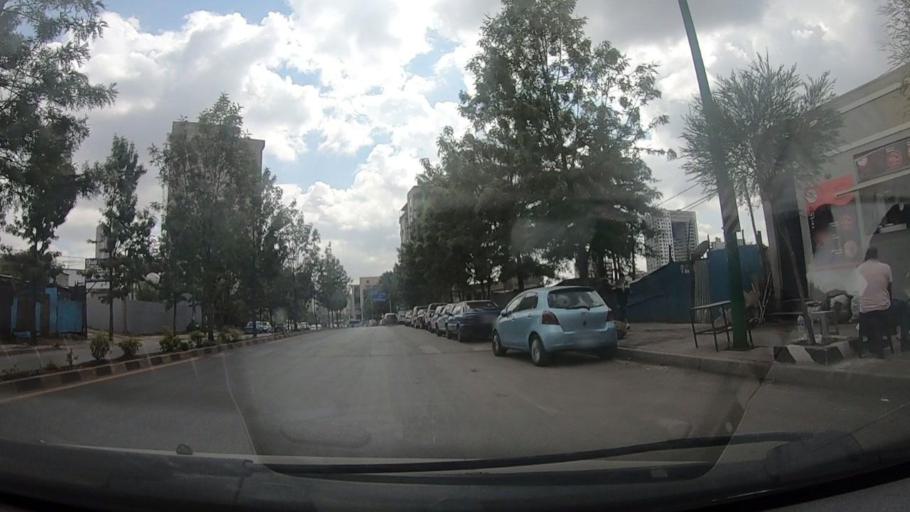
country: ET
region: Adis Abeba
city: Addis Ababa
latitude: 9.0009
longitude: 38.7382
